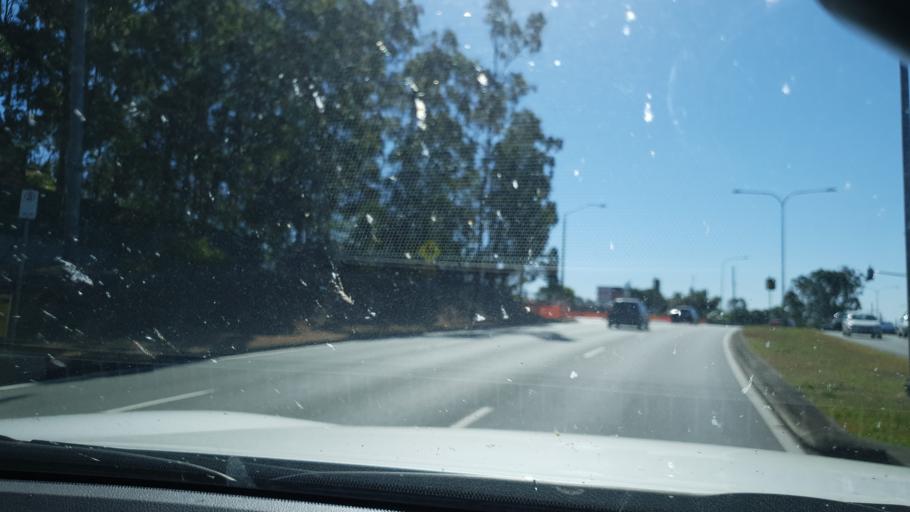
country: AU
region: Queensland
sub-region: Brisbane
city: Bridegman Downs
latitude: -27.3524
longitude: 152.9668
